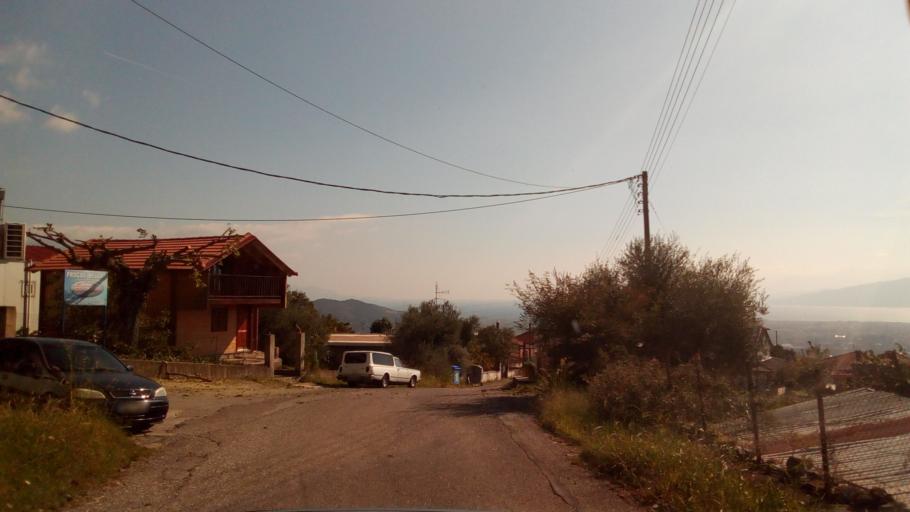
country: GR
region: West Greece
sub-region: Nomos Aitolias kai Akarnanias
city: Nafpaktos
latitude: 38.4230
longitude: 21.8632
